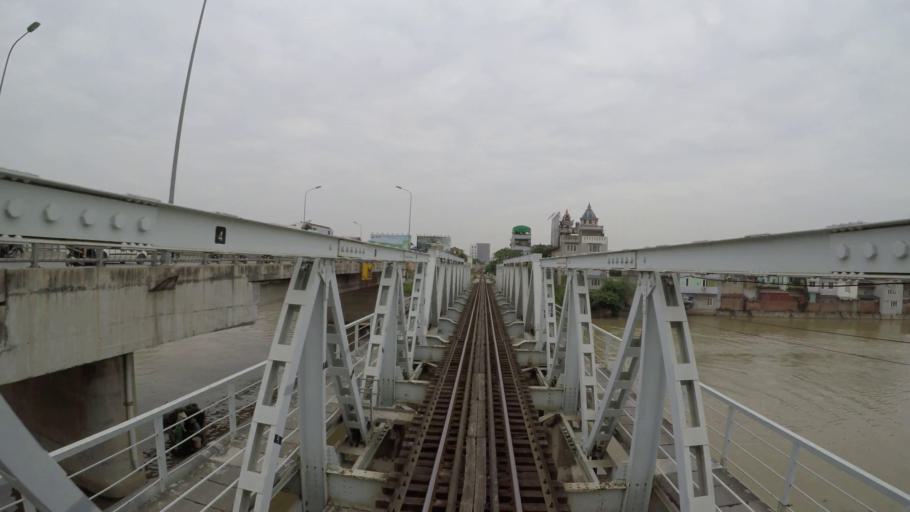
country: VN
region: Hai Phong
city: Haiphong
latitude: 20.8711
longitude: 106.6512
